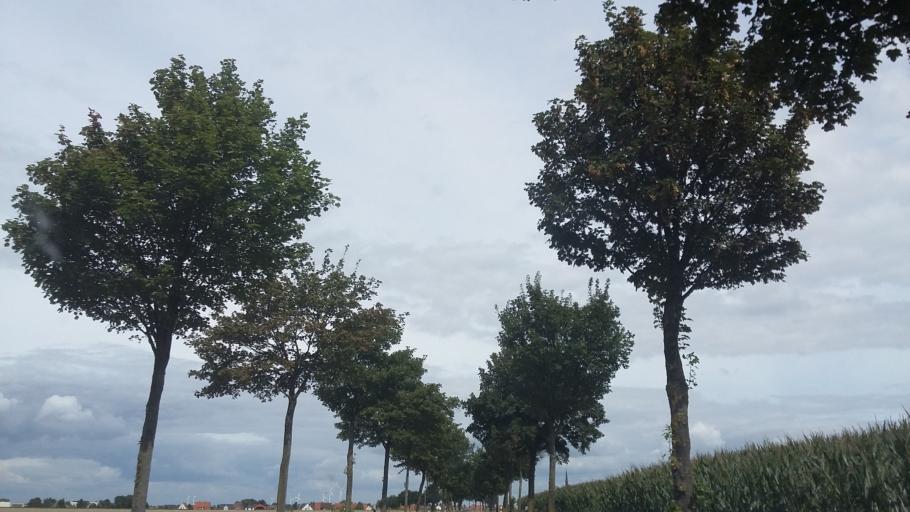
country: DE
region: Lower Saxony
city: Harsum
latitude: 52.1962
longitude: 10.0073
